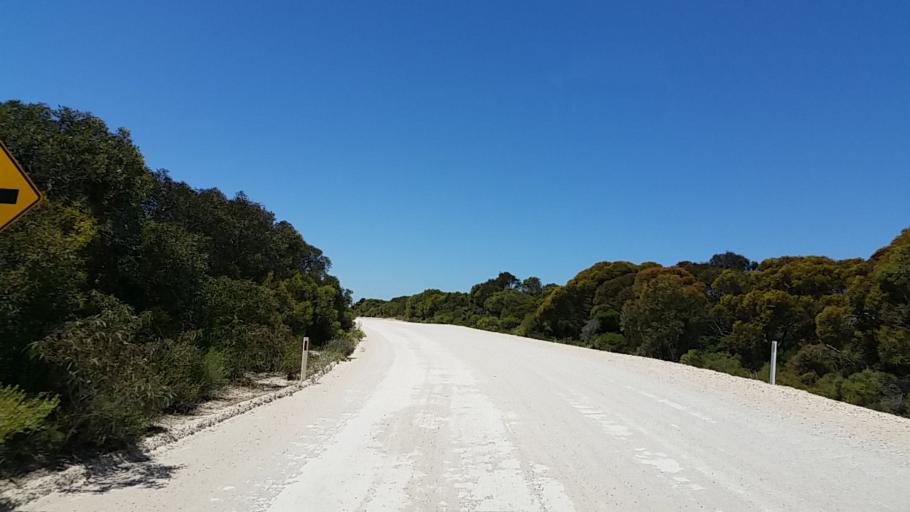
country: AU
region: South Australia
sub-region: Yorke Peninsula
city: Honiton
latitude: -35.2280
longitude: 137.1610
